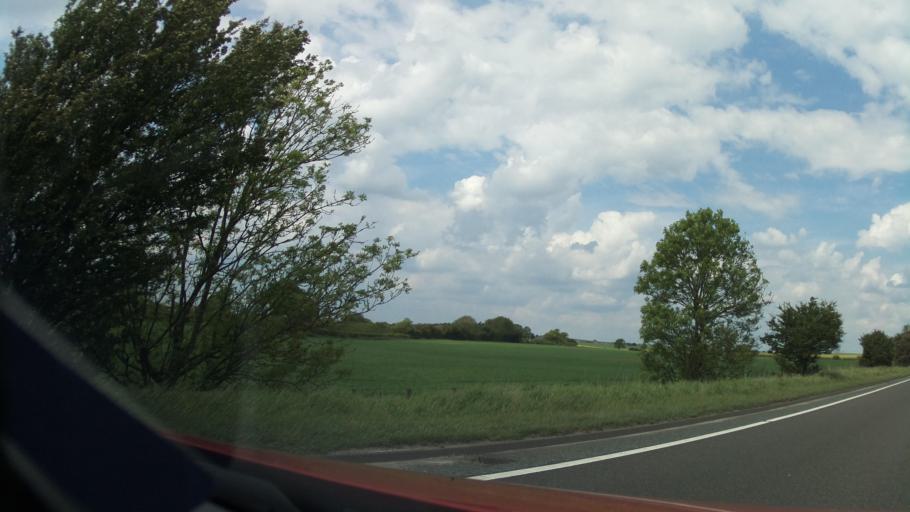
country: GB
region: England
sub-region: North Yorkshire
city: Northallerton
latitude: 54.3412
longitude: -1.3328
